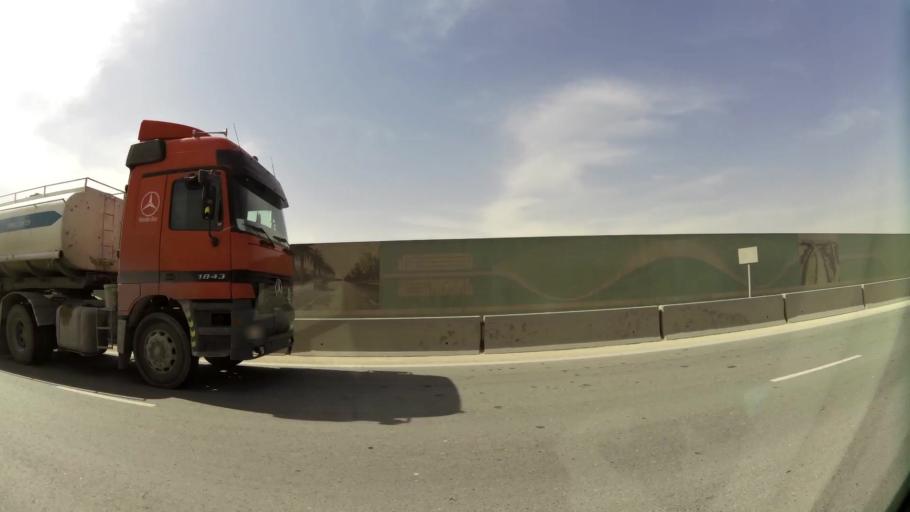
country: QA
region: Baladiyat ar Rayyan
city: Ar Rayyan
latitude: 25.3098
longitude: 51.4096
